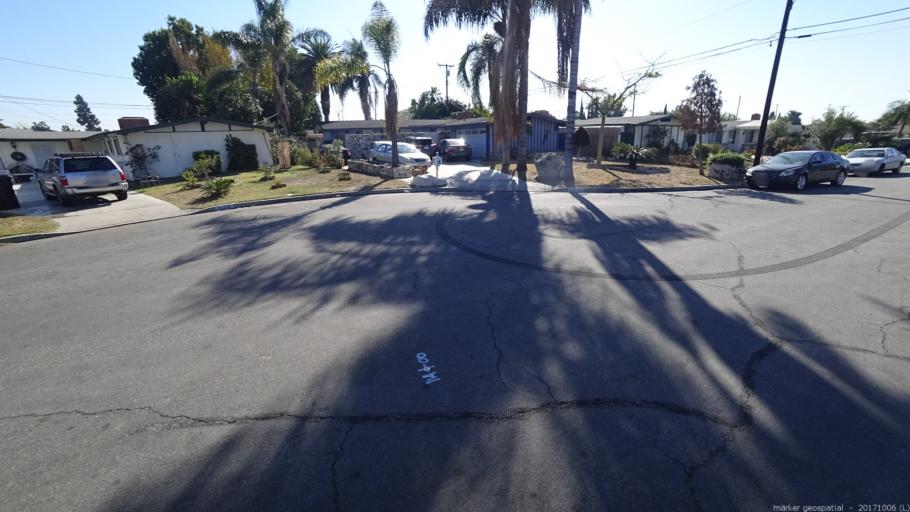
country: US
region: California
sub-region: Orange County
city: Stanton
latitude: 33.7858
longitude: -117.9744
